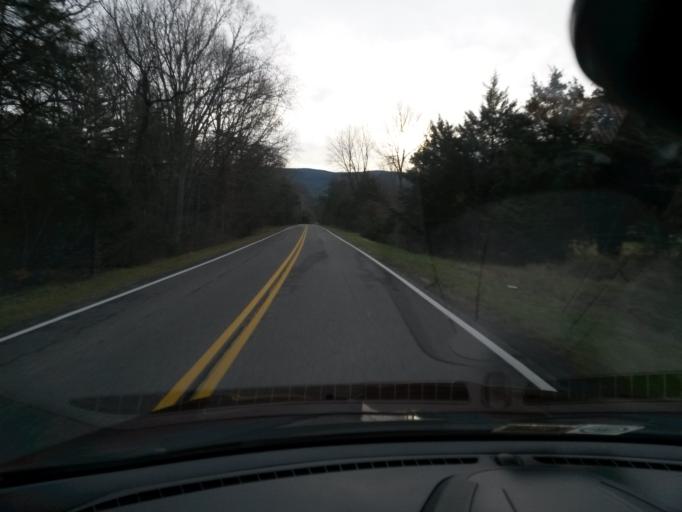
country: US
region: Virginia
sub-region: Alleghany County
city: Clifton Forge
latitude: 37.7980
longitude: -79.7334
